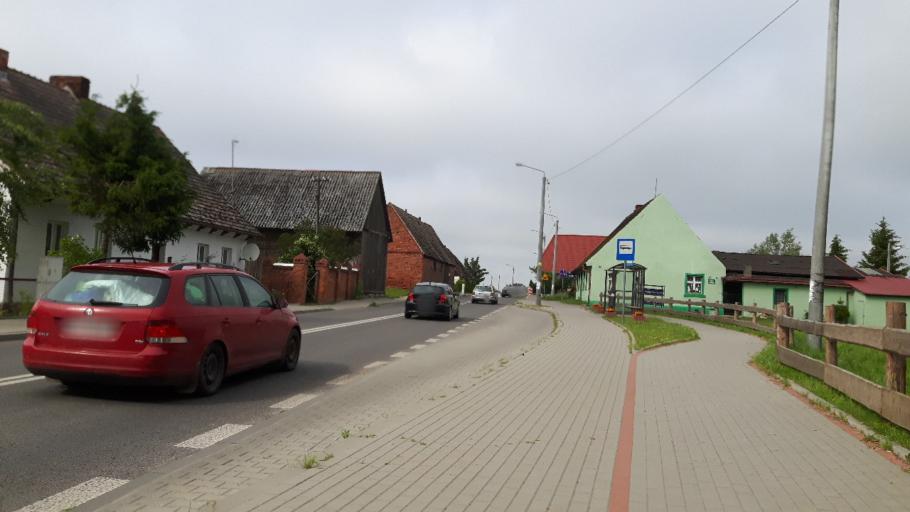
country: PL
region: West Pomeranian Voivodeship
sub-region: Powiat koszalinski
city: Sianow
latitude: 54.3327
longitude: 16.3136
